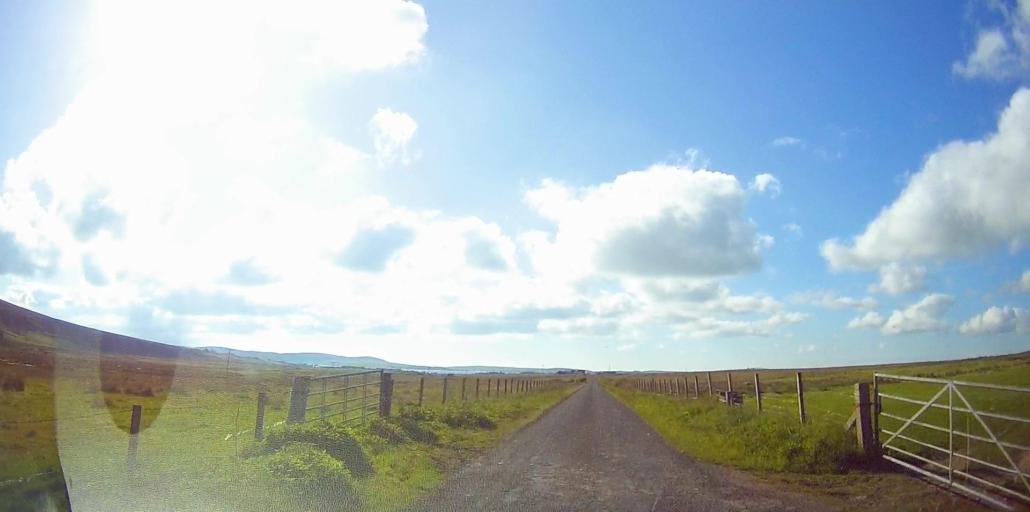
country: GB
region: Scotland
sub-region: Orkney Islands
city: Stromness
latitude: 58.9808
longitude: -3.1784
